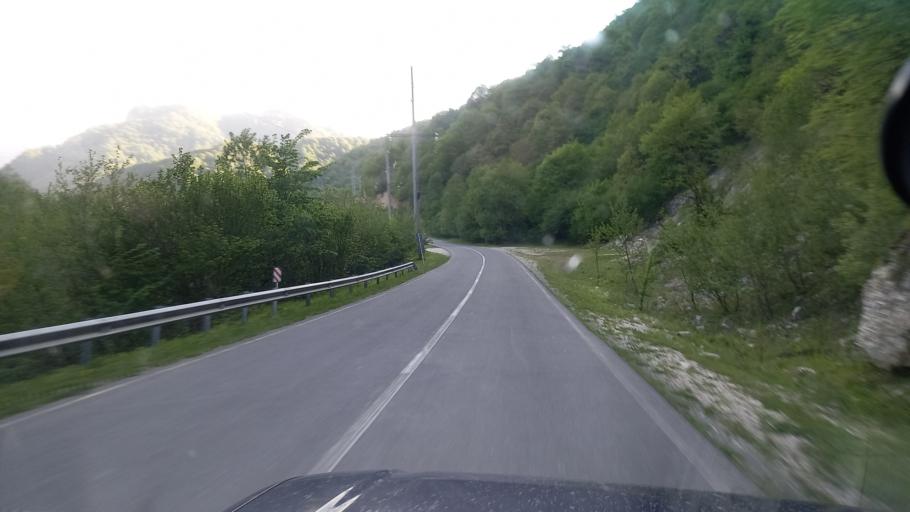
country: RU
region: Ingushetiya
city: Galashki
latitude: 42.9491
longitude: 45.0171
